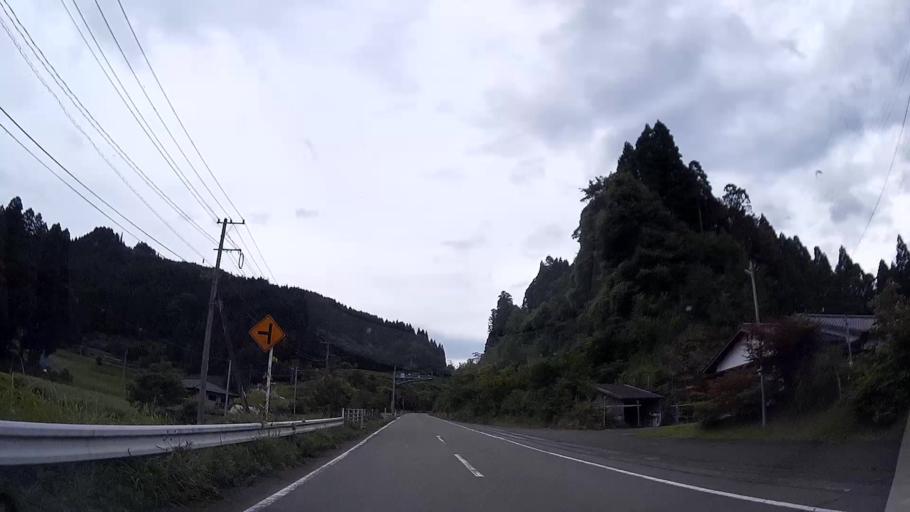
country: JP
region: Oita
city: Hita
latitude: 33.1377
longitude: 130.9843
